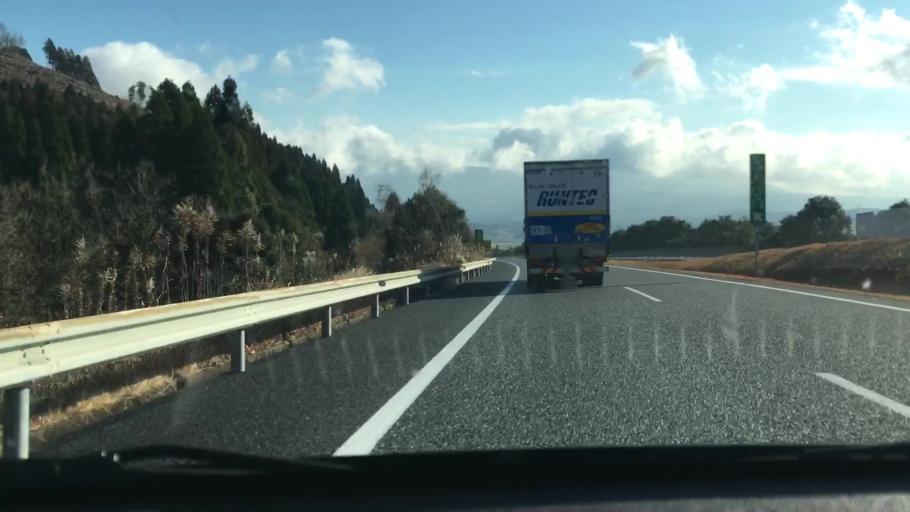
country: JP
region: Kumamoto
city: Hitoyoshi
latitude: 32.0750
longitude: 130.7930
